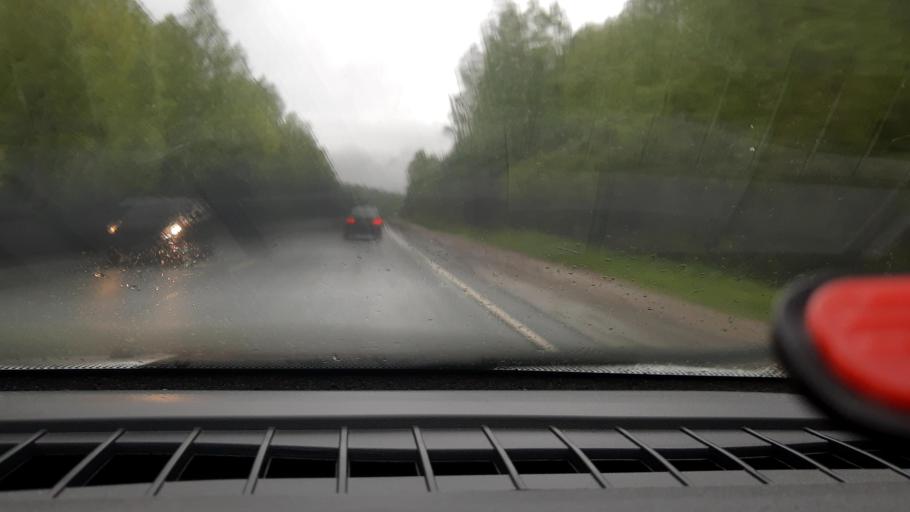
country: RU
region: Nizjnij Novgorod
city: Semenov
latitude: 56.7612
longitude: 44.3762
